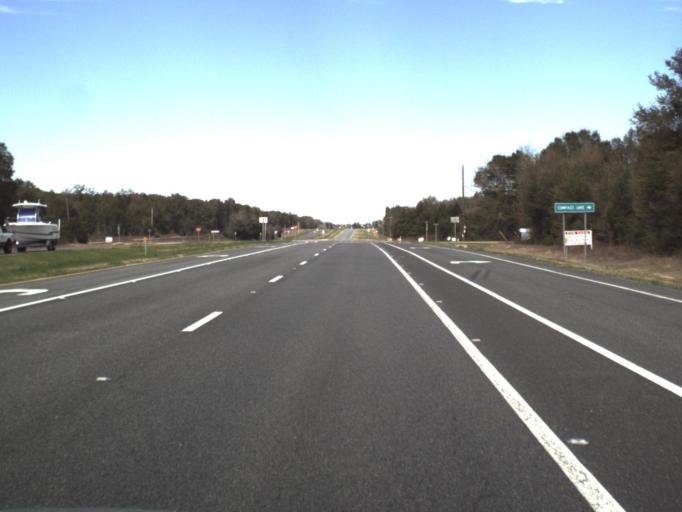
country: US
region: Florida
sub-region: Washington County
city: Chipley
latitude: 30.6302
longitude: -85.3982
